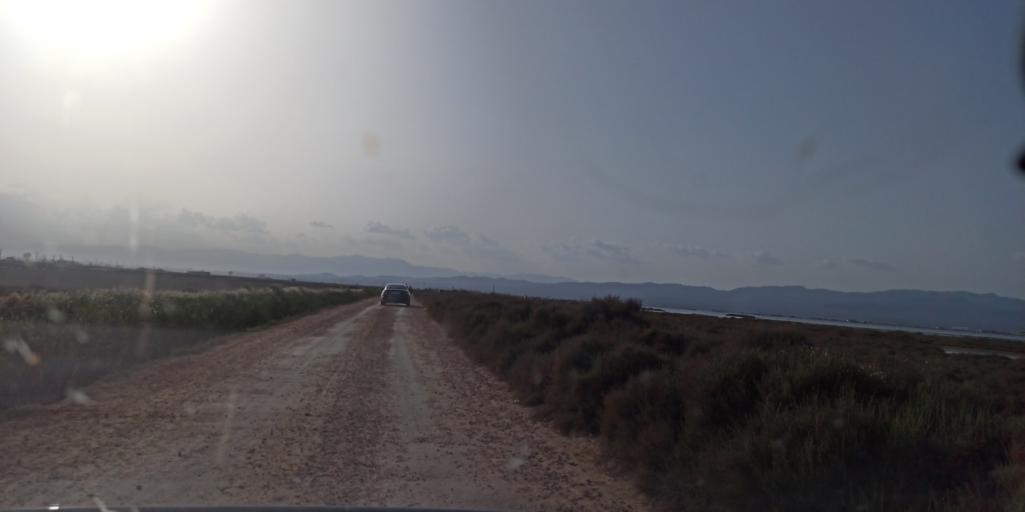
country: ES
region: Catalonia
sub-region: Provincia de Tarragona
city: Deltebre
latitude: 40.7630
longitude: 0.7541
